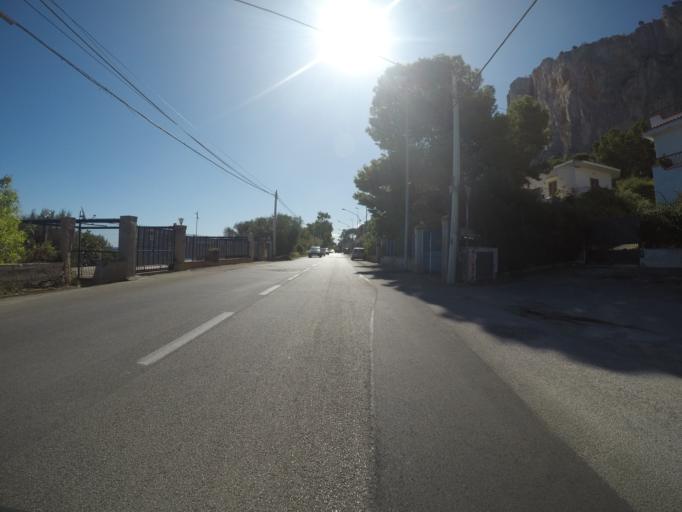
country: IT
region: Sicily
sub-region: Palermo
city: Palermo
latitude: 38.1860
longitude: 13.3615
